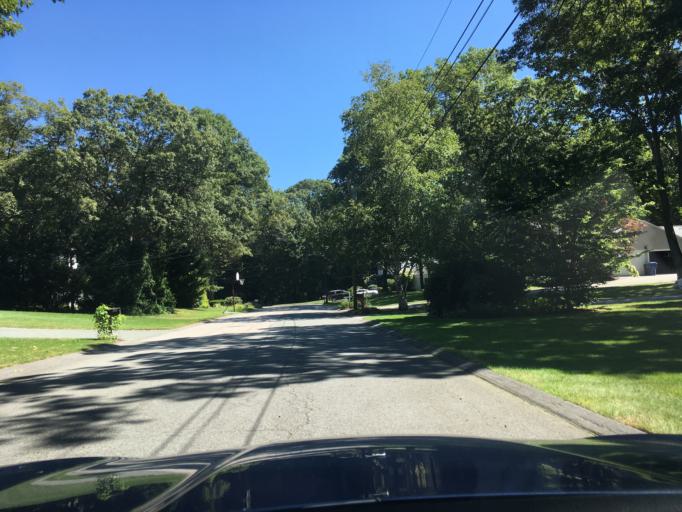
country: US
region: Rhode Island
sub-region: Kent County
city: East Greenwich
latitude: 41.6370
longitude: -71.4748
